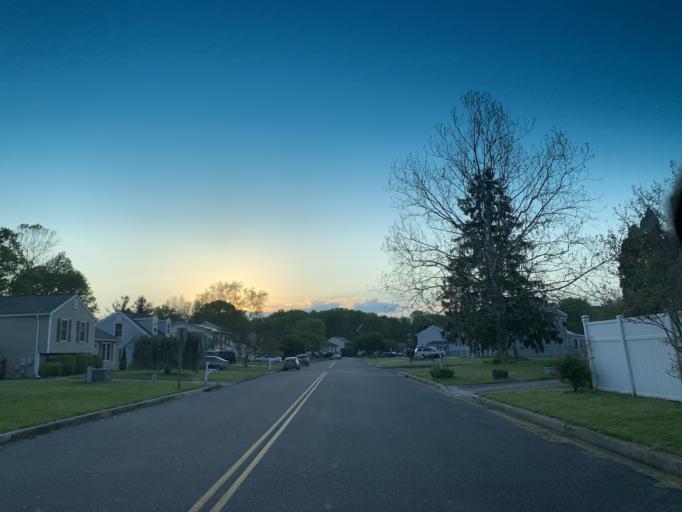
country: US
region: Maryland
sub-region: Harford County
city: Aberdeen
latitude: 39.4982
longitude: -76.1820
